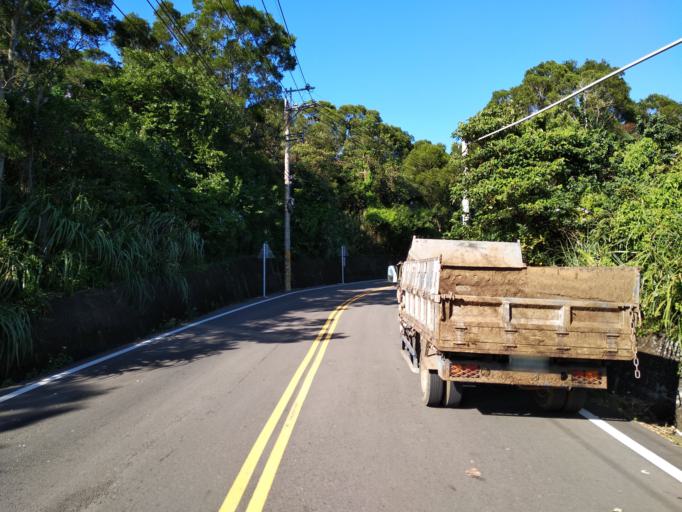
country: TW
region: Taiwan
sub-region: Hsinchu
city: Zhubei
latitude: 24.8644
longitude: 121.0951
